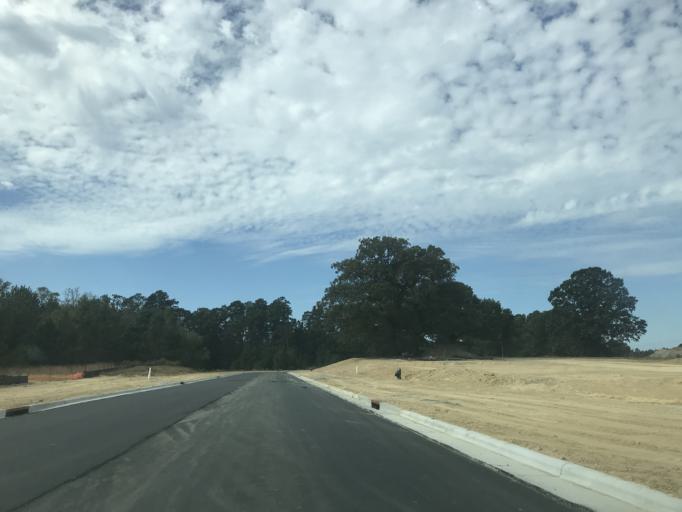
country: US
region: North Carolina
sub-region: Wake County
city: Knightdale
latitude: 35.8604
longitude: -78.5433
